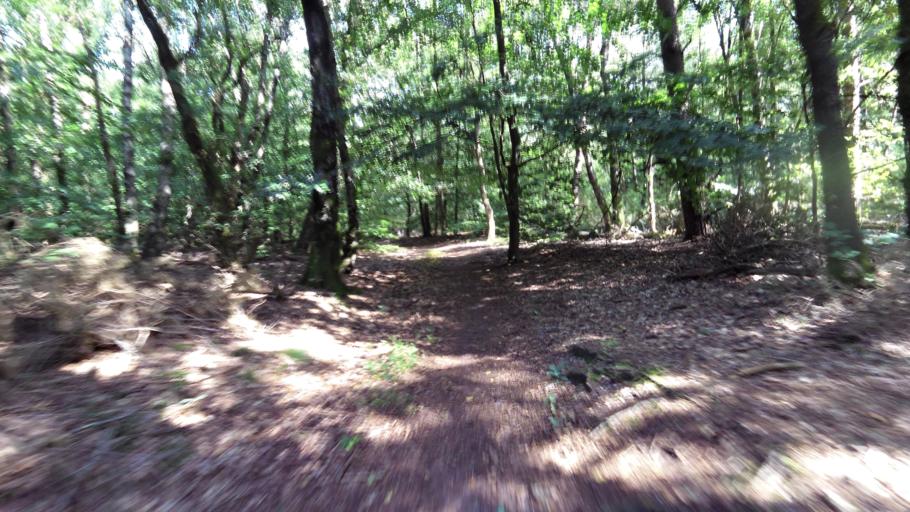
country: NL
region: Gelderland
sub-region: Gemeente Ede
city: Bennekom
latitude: 52.0128
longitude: 5.7032
